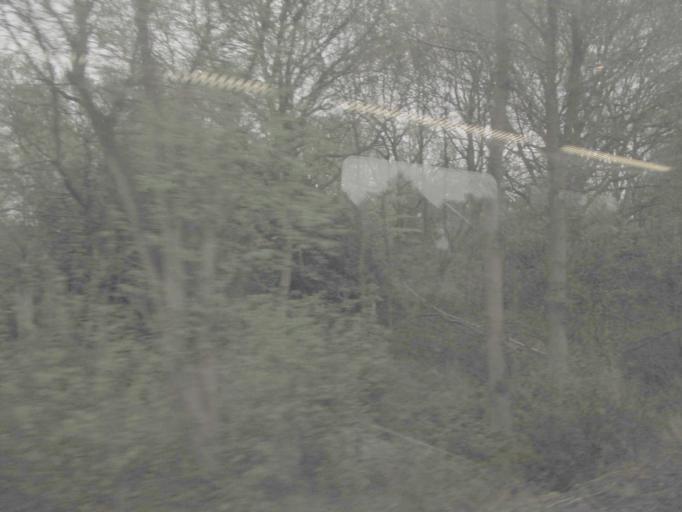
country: GB
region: England
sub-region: Bracknell Forest
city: Sandhurst
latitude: 51.3284
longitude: -0.7734
